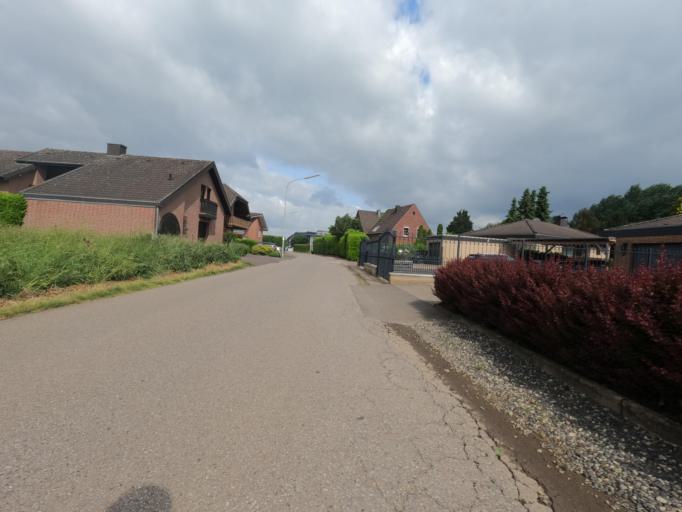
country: DE
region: North Rhine-Westphalia
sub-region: Regierungsbezirk Koln
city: Wassenberg
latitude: 51.0881
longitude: 6.1234
